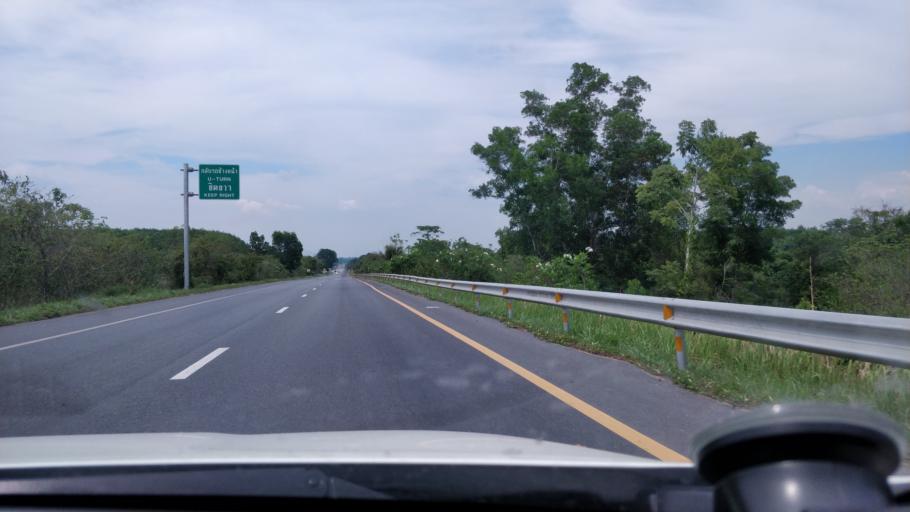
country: TH
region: Surat Thani
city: Khian Sa
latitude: 8.8298
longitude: 99.1730
